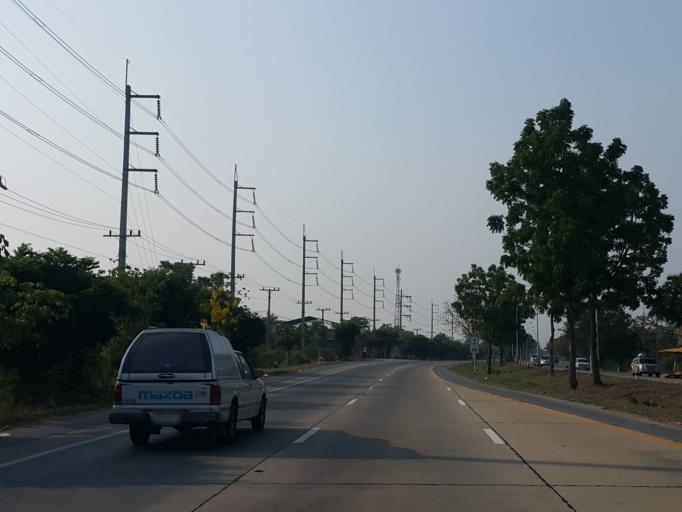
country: TH
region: Suphan Buri
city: Doem Bang Nang Buat
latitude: 14.9317
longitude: 100.0836
